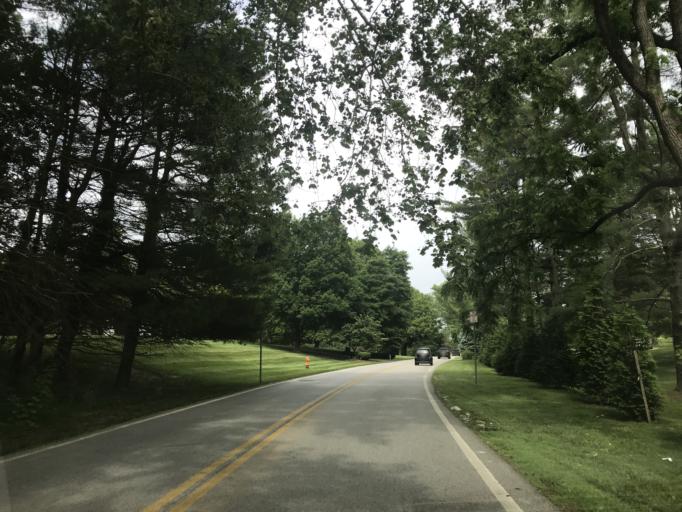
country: US
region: Maryland
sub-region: Baltimore County
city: Hampton
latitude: 39.4253
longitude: -76.5941
